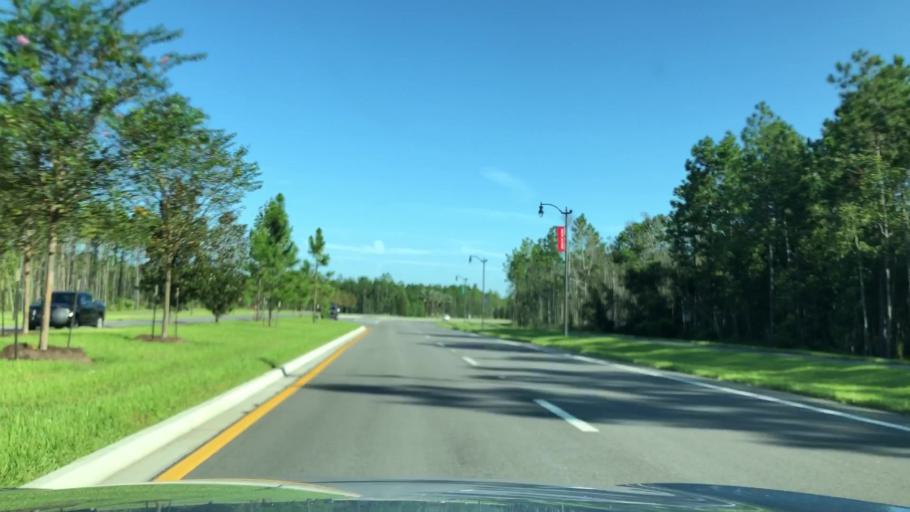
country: US
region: Florida
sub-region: Saint Johns County
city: Palm Valley
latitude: 30.0824
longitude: -81.4037
